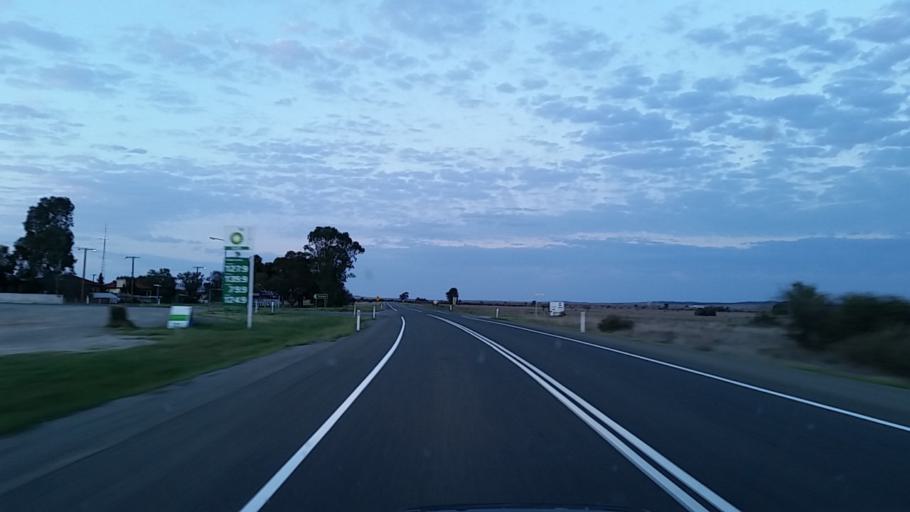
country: AU
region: South Australia
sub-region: Peterborough
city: Peterborough
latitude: -33.1541
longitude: 138.9223
